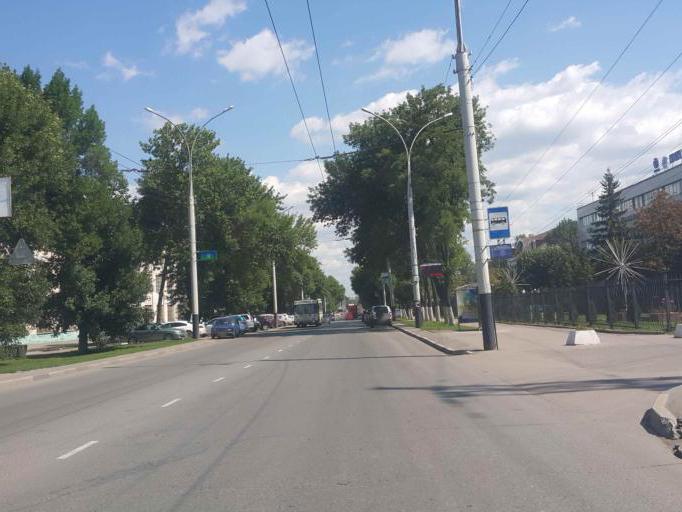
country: RU
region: Tambov
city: Donskoye
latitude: 52.7541
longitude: 41.4684
